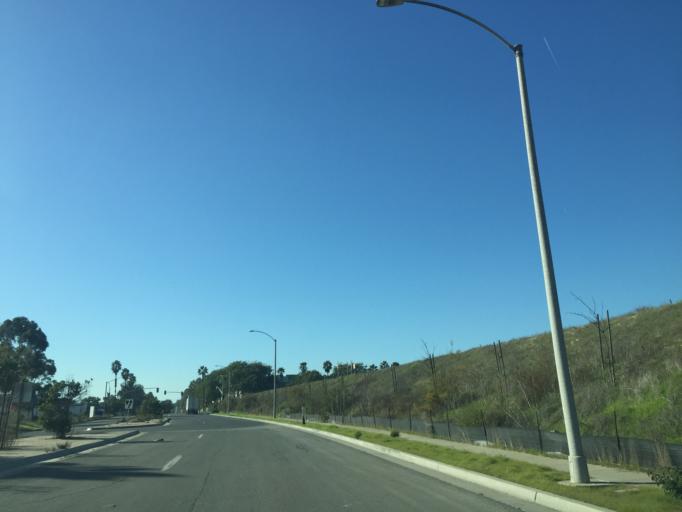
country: MX
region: Baja California
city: Tijuana
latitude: 32.5568
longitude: -116.9257
